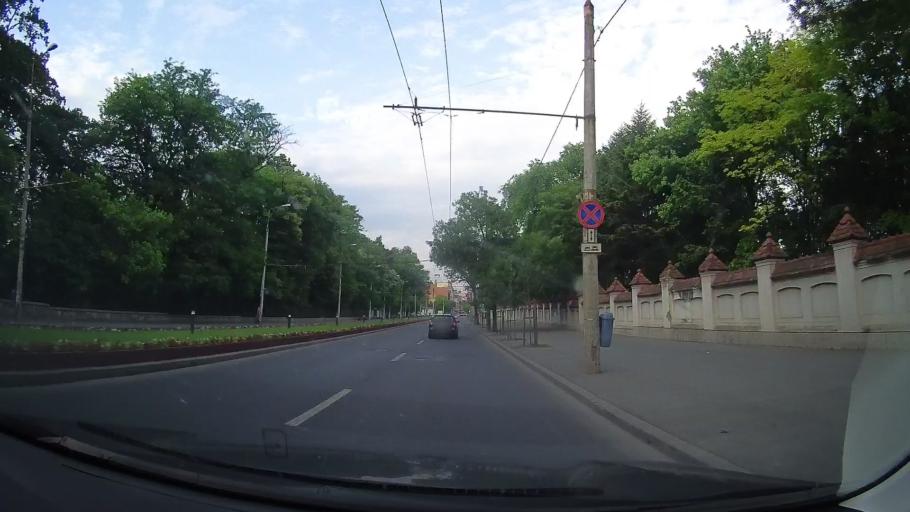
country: RO
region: Bucuresti
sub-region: Municipiul Bucuresti
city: Bucuresti
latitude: 44.4358
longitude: 26.0645
